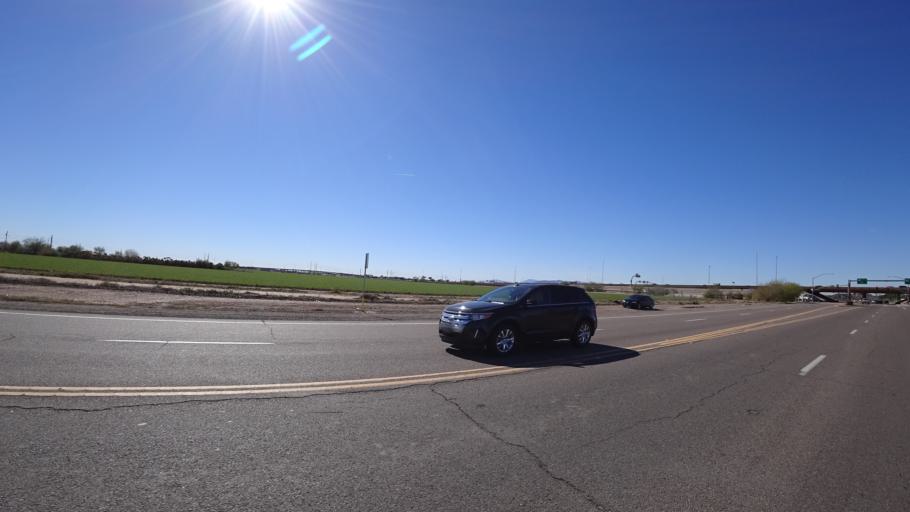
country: US
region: Arizona
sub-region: Maricopa County
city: Tempe
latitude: 33.4514
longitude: -111.8877
